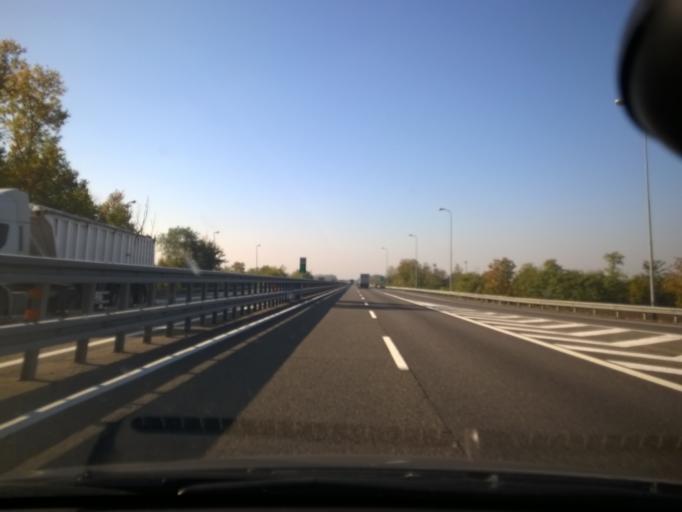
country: IT
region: Lombardy
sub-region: Provincia di Pavia
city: Stradella
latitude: 45.0833
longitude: 9.3119
